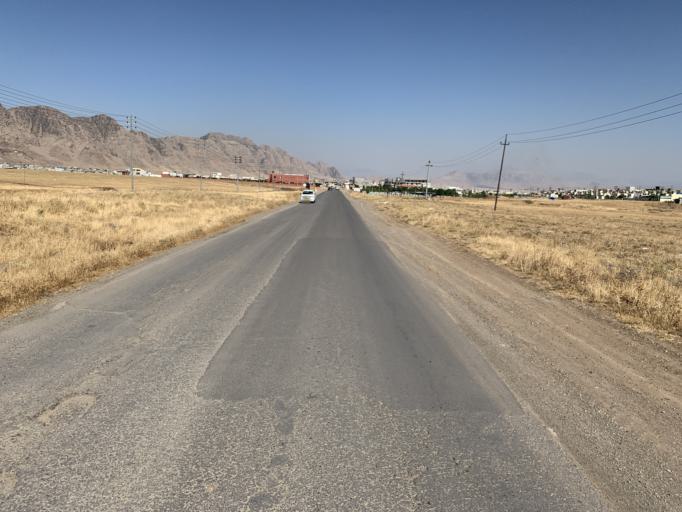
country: IQ
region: As Sulaymaniyah
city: Raniye
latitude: 36.2630
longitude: 44.8495
